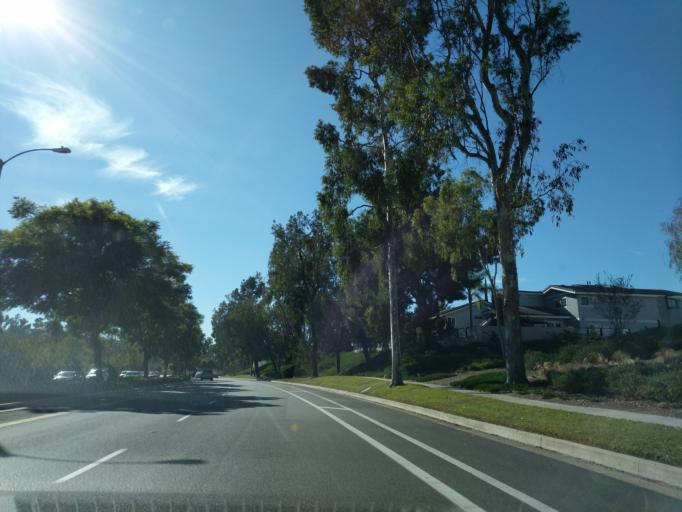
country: US
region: California
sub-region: Orange County
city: Irvine
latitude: 33.6584
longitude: -117.8081
